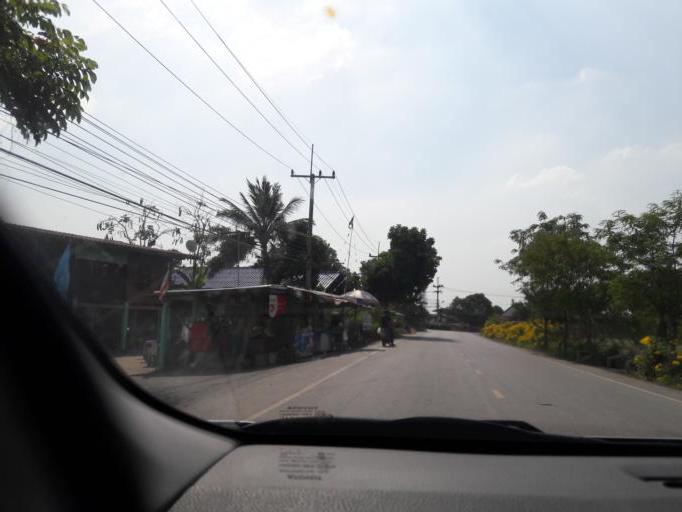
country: TH
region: Ang Thong
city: Ang Thong
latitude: 14.5855
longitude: 100.4297
